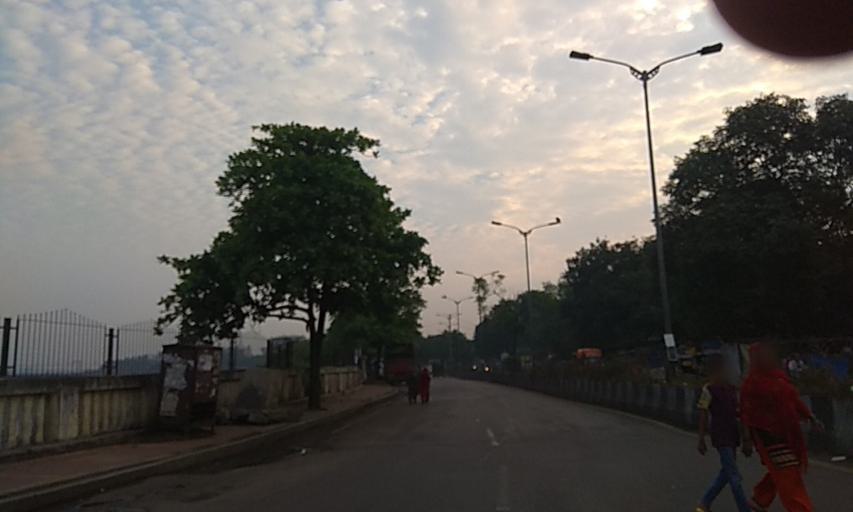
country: IN
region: Maharashtra
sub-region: Pune Division
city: Pune
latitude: 18.5241
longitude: 73.8581
